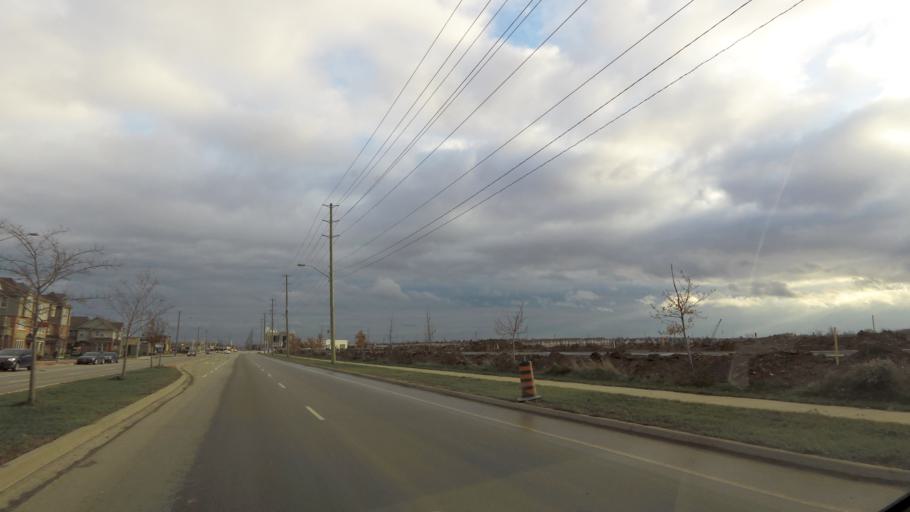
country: CA
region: Ontario
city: Burlington
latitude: 43.3943
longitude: -79.8268
